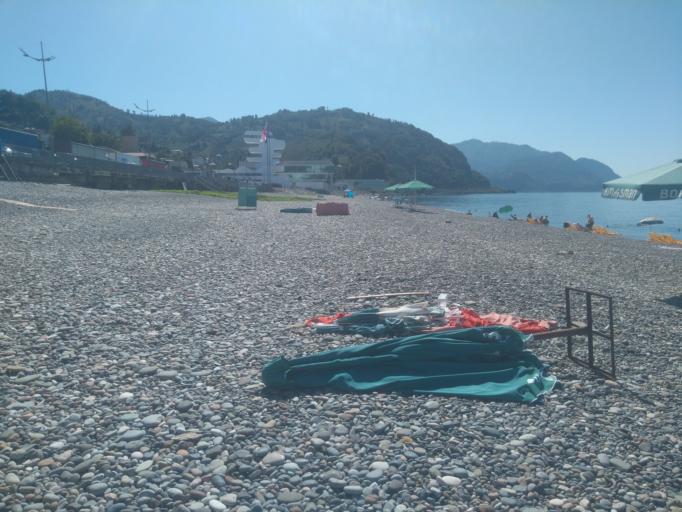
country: TR
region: Artvin
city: Kemalpasa
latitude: 41.5245
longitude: 41.5485
